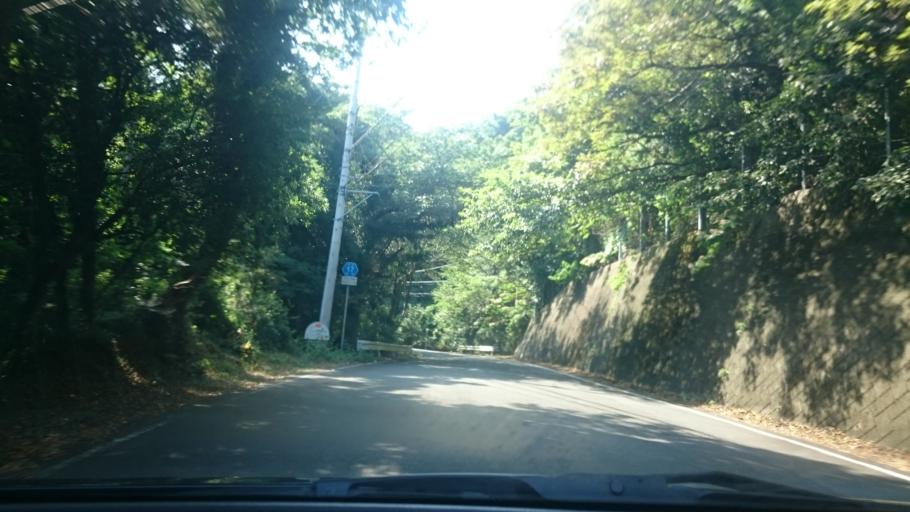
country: JP
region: Shizuoka
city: Heda
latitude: 34.9265
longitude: 138.7825
